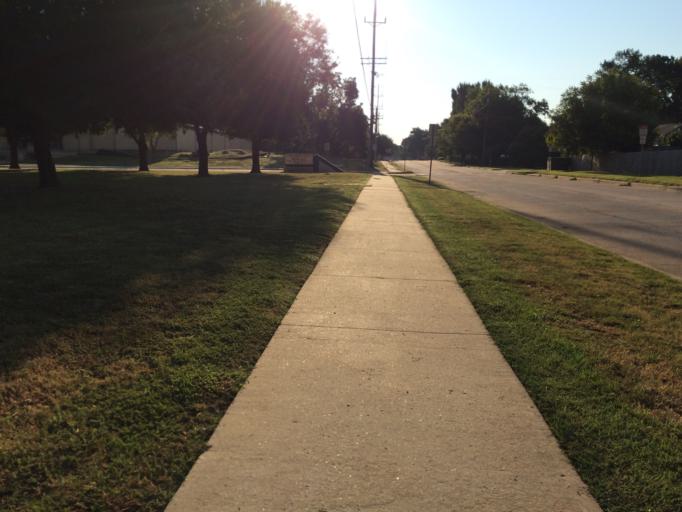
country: US
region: Oklahoma
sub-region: Cleveland County
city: Norman
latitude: 35.2112
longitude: -97.4708
